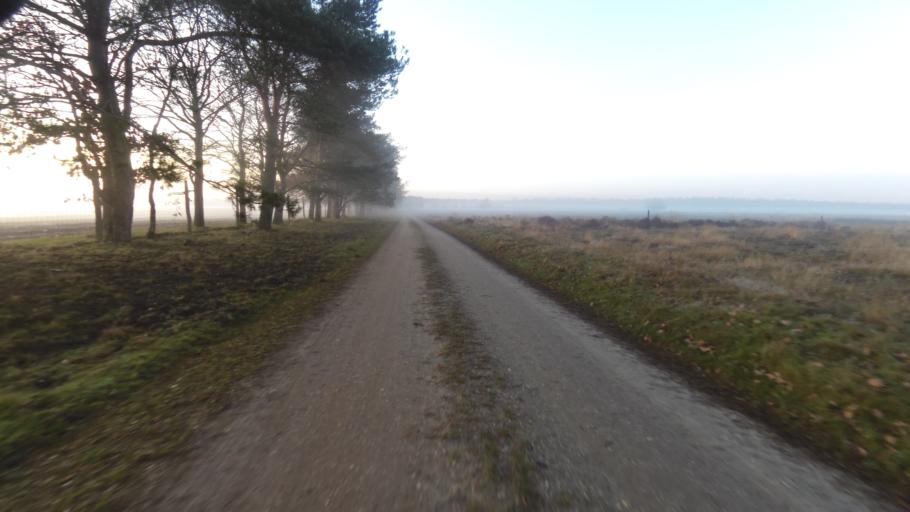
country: NL
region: Gelderland
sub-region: Gemeente Apeldoorn
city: Uddel
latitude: 52.2432
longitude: 5.7897
